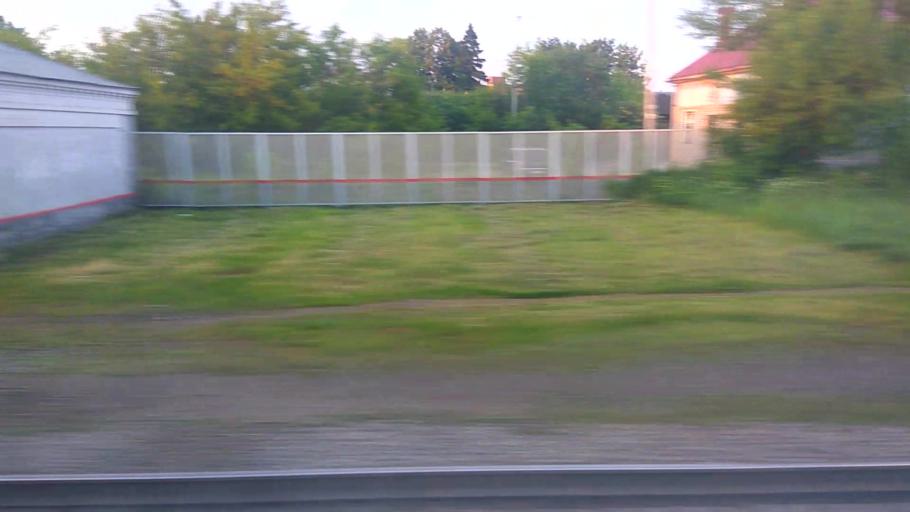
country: RU
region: Moskovskaya
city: Barybino
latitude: 55.2735
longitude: 37.8946
